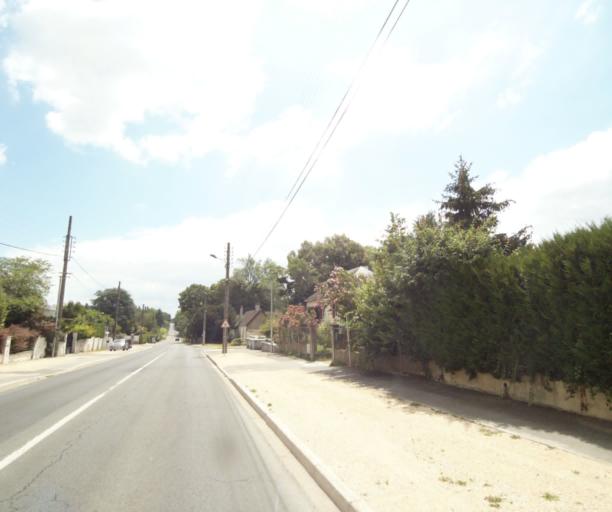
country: FR
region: Centre
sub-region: Departement du Loiret
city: Saint-Jean-de-Braye
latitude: 47.9064
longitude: 1.9854
